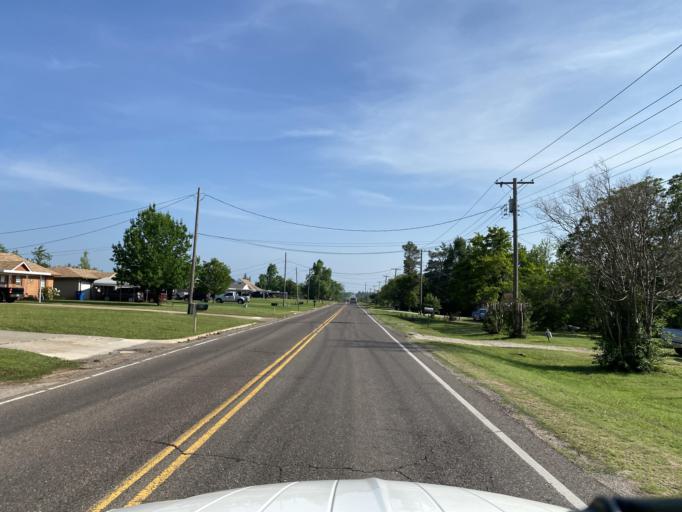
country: US
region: Oklahoma
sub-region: Oklahoma County
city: Nicoma Park
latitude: 35.4826
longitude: -97.3356
